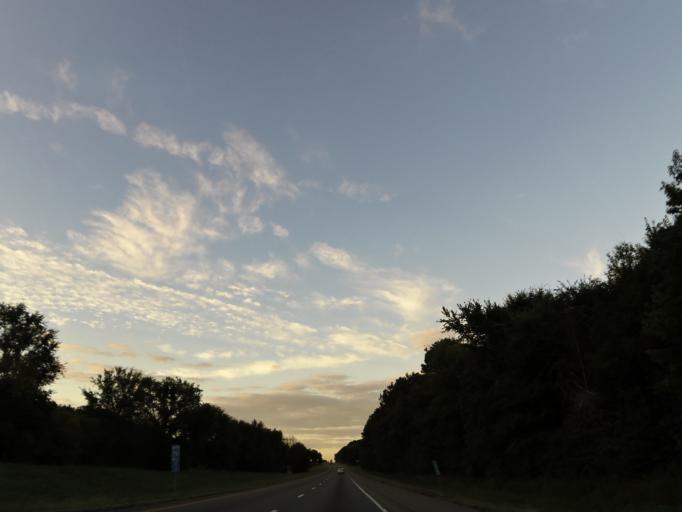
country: US
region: Tennessee
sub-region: McMinn County
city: Athens
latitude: 35.5142
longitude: -84.5999
